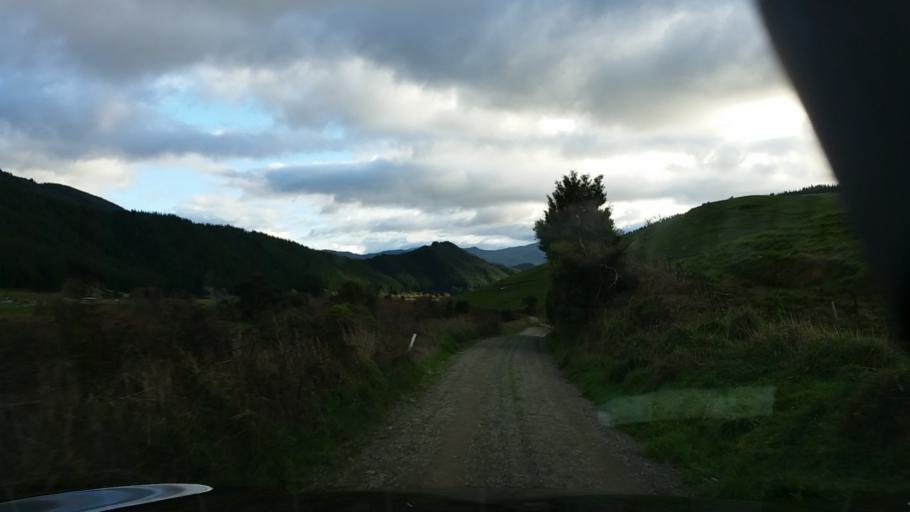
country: NZ
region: Nelson
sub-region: Nelson City
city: Nelson
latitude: -41.2080
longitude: 173.6370
